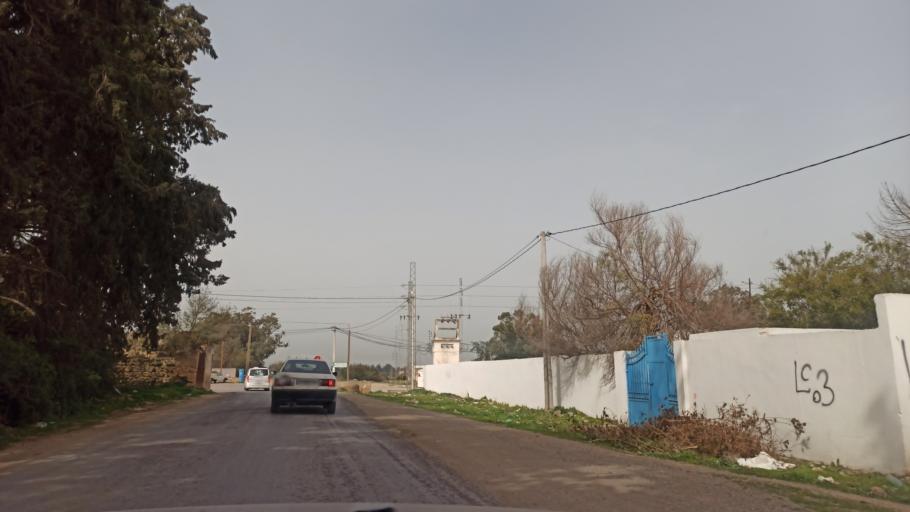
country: TN
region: Zaghwan
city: Zaghouan
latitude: 36.4234
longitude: 10.0941
